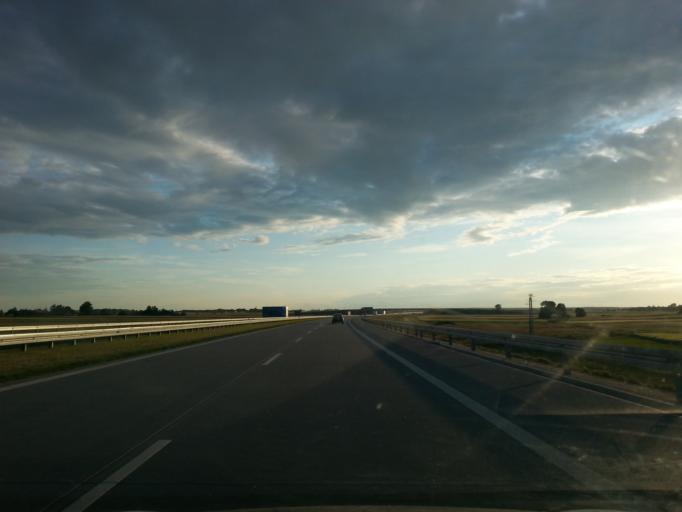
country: PL
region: Lodz Voivodeship
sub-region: Powiat wieruszowski
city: Walichnowy
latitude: 51.3153
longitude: 18.4134
